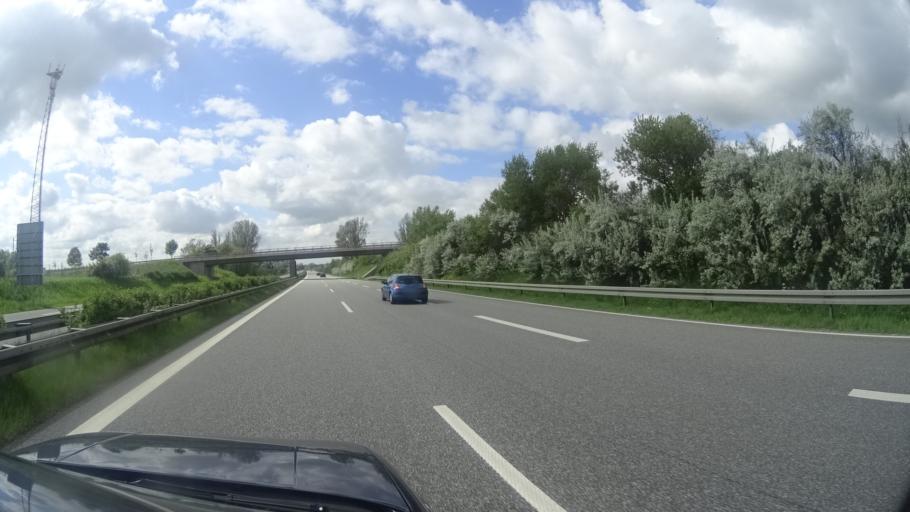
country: DE
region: Mecklenburg-Vorpommern
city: Laage
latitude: 53.8430
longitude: 12.2847
